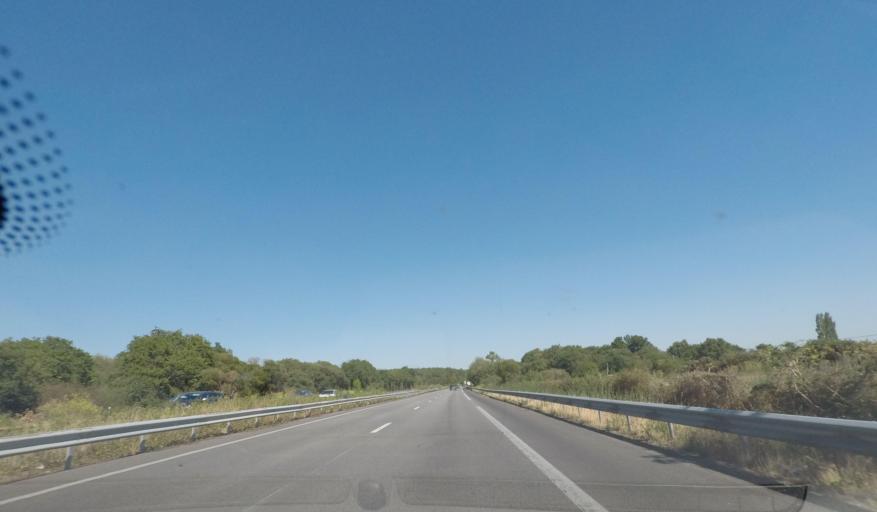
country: FR
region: Brittany
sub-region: Departement du Morbihan
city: Marzan
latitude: 47.5383
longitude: -2.3641
